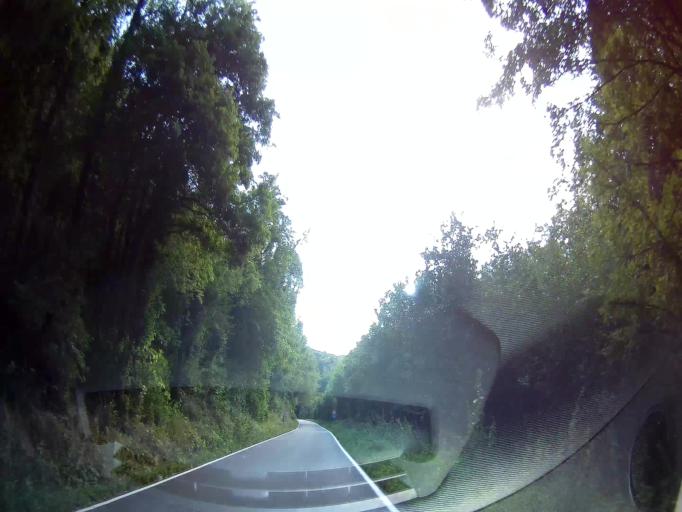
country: BE
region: Wallonia
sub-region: Province de Namur
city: Onhaye
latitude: 50.3027
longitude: 4.7795
